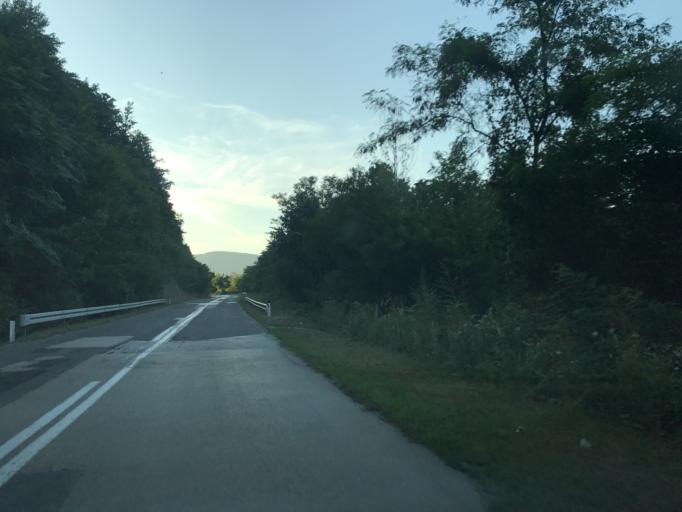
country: RO
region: Caras-Severin
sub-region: Comuna Berzasca
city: Berzasca
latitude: 44.6272
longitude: 21.9907
